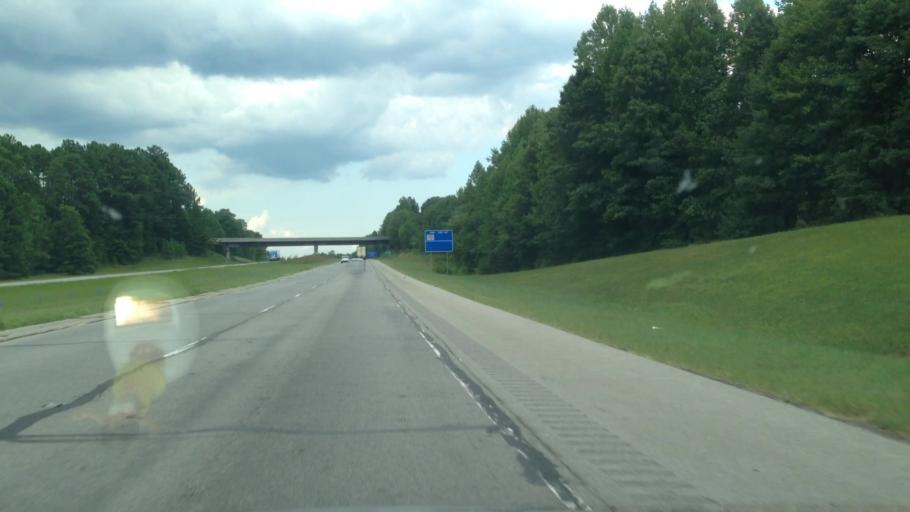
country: US
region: Virginia
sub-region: City of Danville
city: Danville
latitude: 36.5058
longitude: -79.4792
